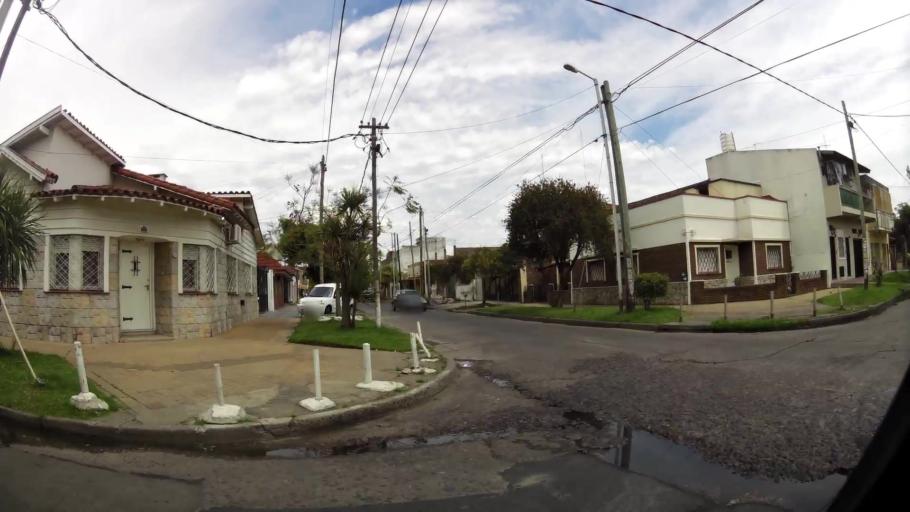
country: AR
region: Buenos Aires
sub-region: Partido de Avellaneda
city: Avellaneda
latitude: -34.6785
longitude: -58.3725
